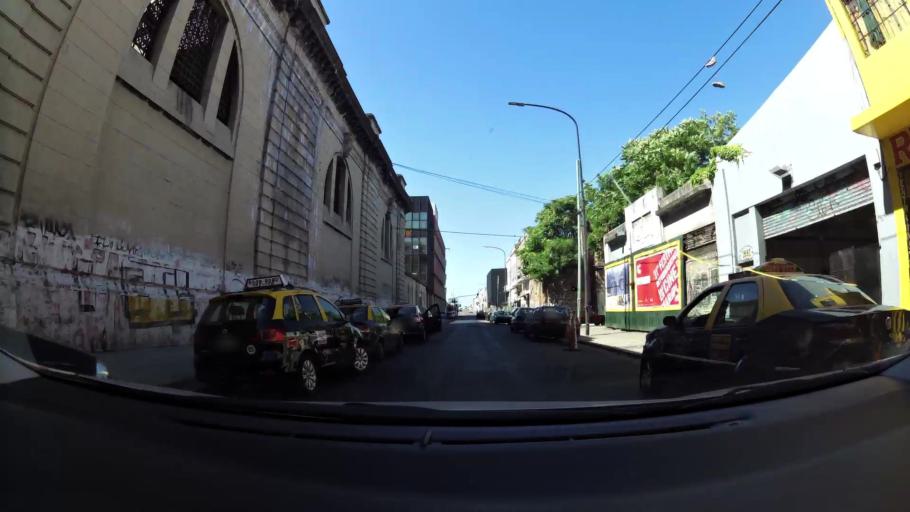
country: AR
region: Buenos Aires F.D.
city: Buenos Aires
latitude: -34.6298
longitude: -58.3814
